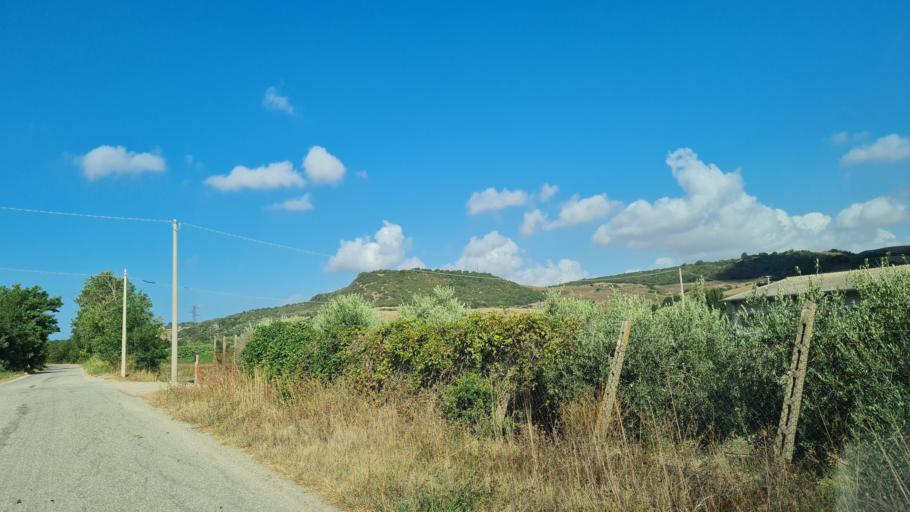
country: IT
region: Latium
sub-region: Provincia di Viterbo
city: Tarquinia
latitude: 42.2611
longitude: 11.7592
